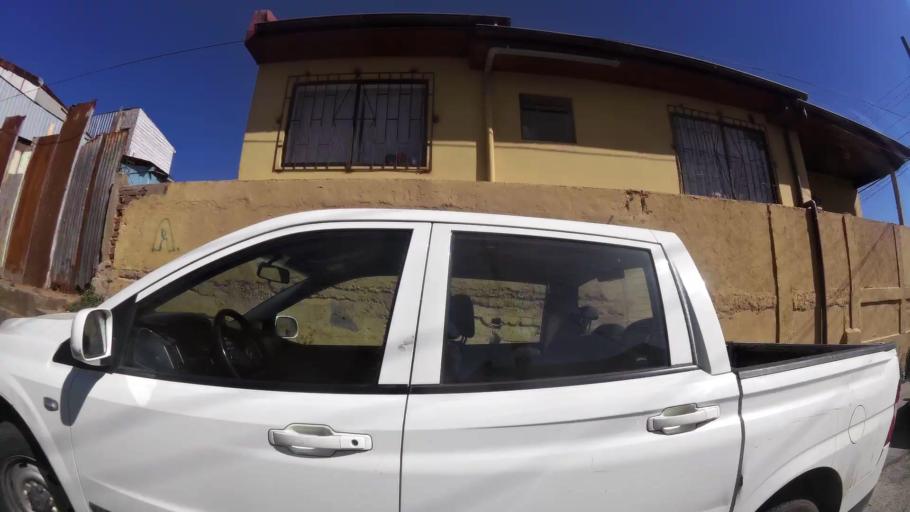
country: CL
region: Valparaiso
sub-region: Provincia de Valparaiso
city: Valparaiso
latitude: -33.0445
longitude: -71.6371
